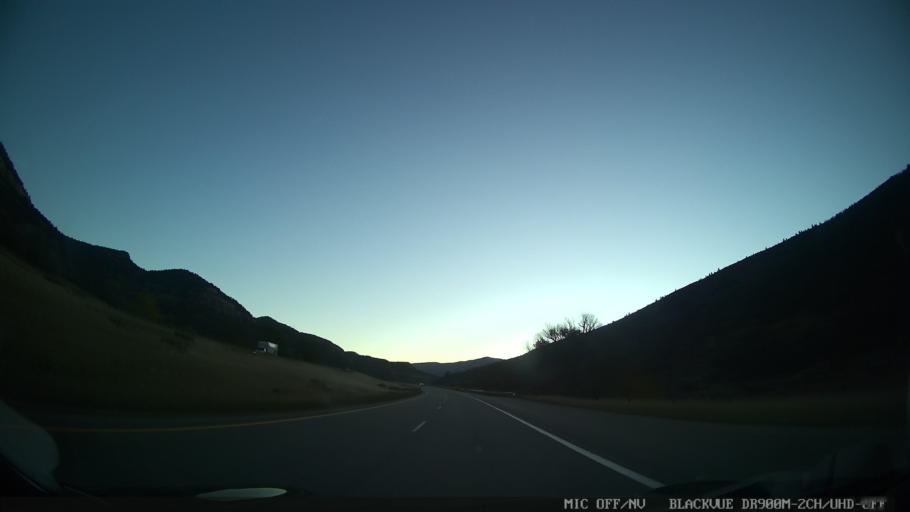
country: US
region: Colorado
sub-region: Eagle County
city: Eagle
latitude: 39.7062
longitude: -106.7232
